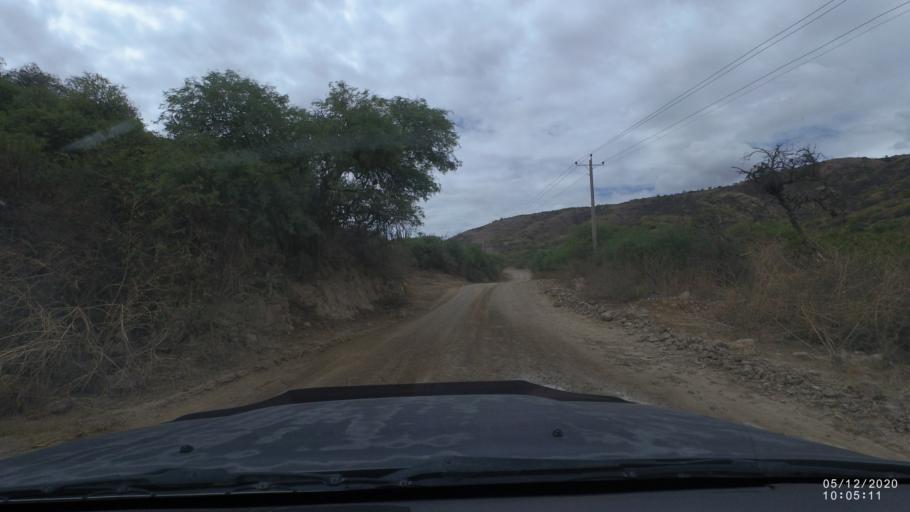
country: BO
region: Cochabamba
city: Sipe Sipe
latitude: -17.4685
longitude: -66.2850
